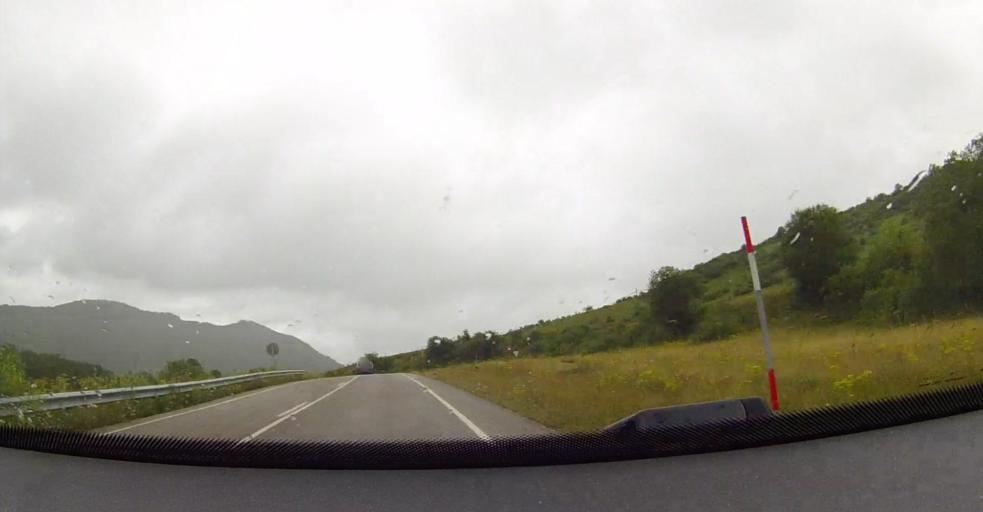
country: ES
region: Castille and Leon
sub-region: Provincia de Leon
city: Acebedo
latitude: 43.0446
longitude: -5.1232
